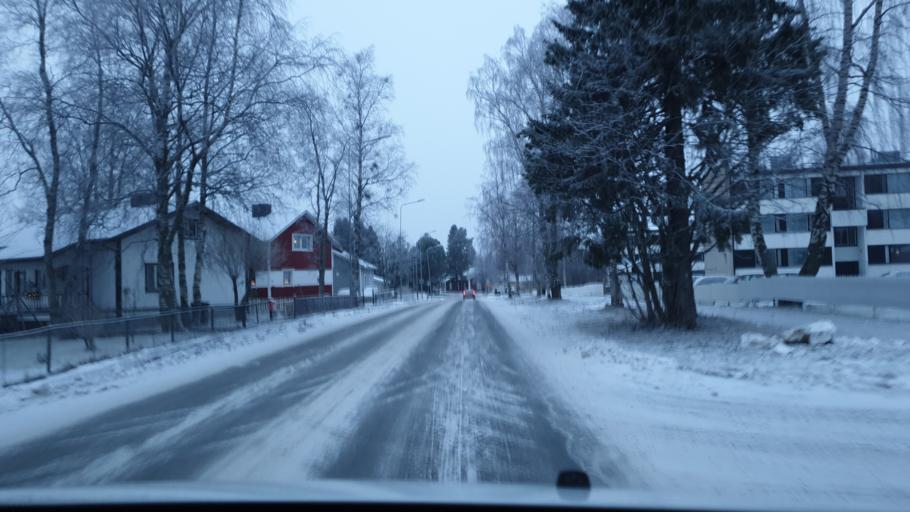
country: FI
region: Lapland
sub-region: Kemi-Tornio
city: Kemi
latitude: 65.7318
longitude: 24.6010
